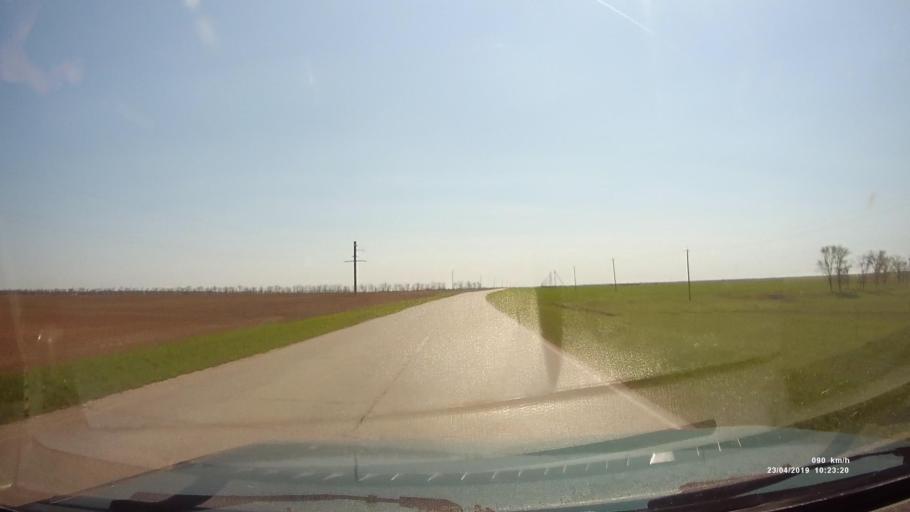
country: RU
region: Rostov
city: Sovetskoye
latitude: 46.6484
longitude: 42.4225
